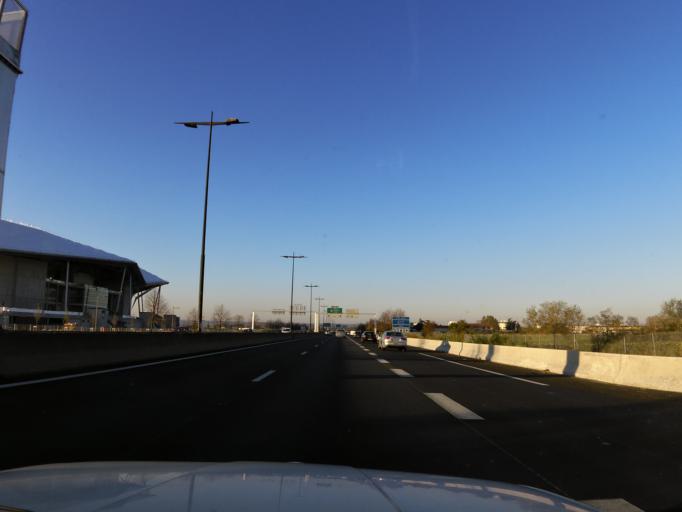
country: FR
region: Rhone-Alpes
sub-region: Departement du Rhone
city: Decines-Charpieu
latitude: 45.7630
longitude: 4.9851
